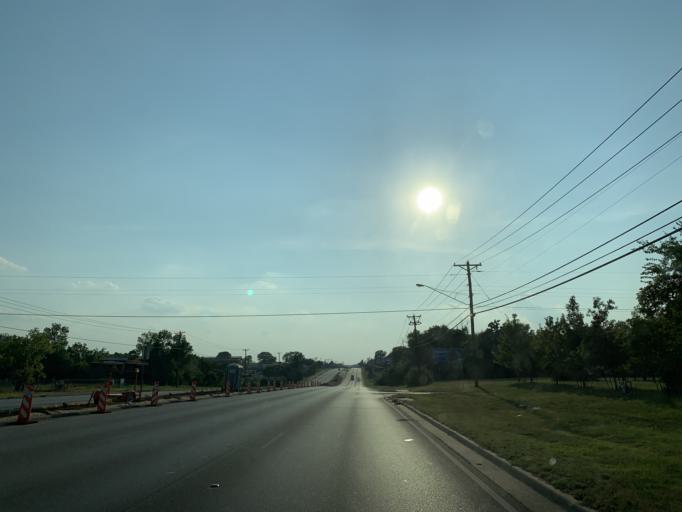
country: US
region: Texas
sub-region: Tarrant County
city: Hurst
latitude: 32.8091
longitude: -97.1760
